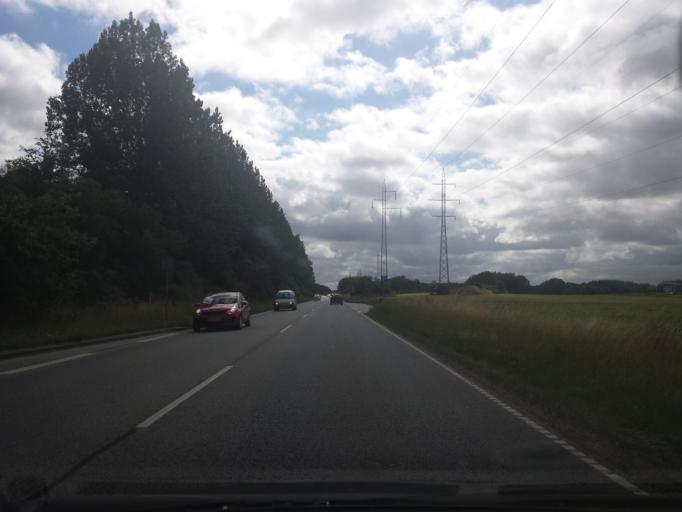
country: DK
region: South Denmark
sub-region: Sonderborg Kommune
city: Sonderborg
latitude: 54.9290
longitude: 9.7944
